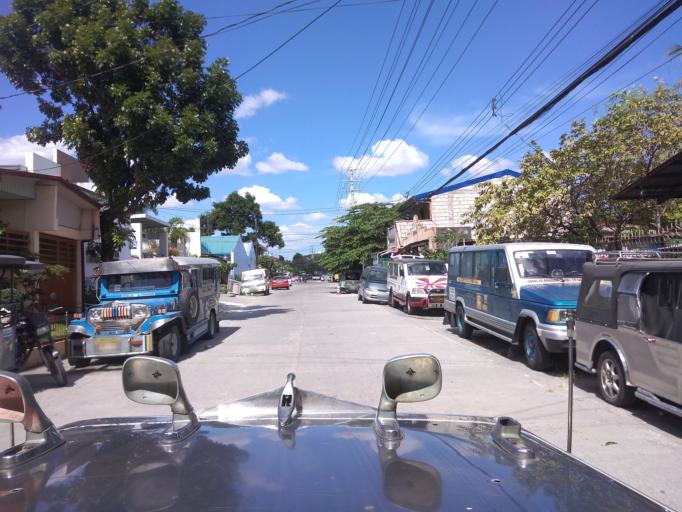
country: PH
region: Central Luzon
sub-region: Province of Pampanga
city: Calibutbut
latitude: 15.1183
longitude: 120.6018
